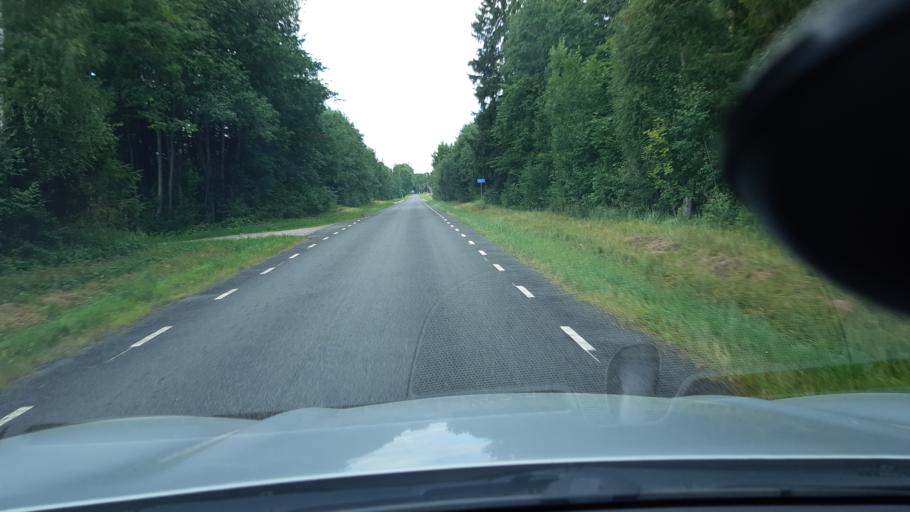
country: EE
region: Raplamaa
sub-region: Jaervakandi vald
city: Jarvakandi
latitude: 58.8711
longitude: 24.7627
